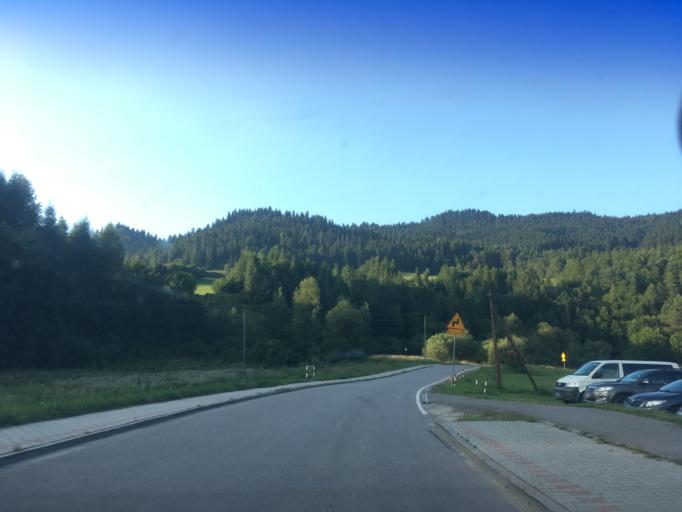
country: PL
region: Lesser Poland Voivodeship
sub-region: Powiat nowotarski
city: Krosnica
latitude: 49.4073
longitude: 20.3665
